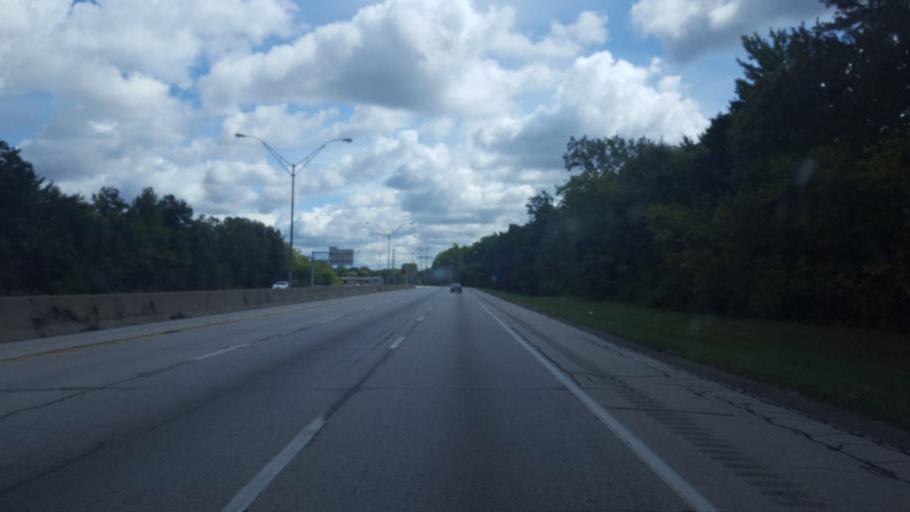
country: US
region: Ohio
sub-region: Cuyahoga County
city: North Olmsted
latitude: 41.3890
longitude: -81.9642
